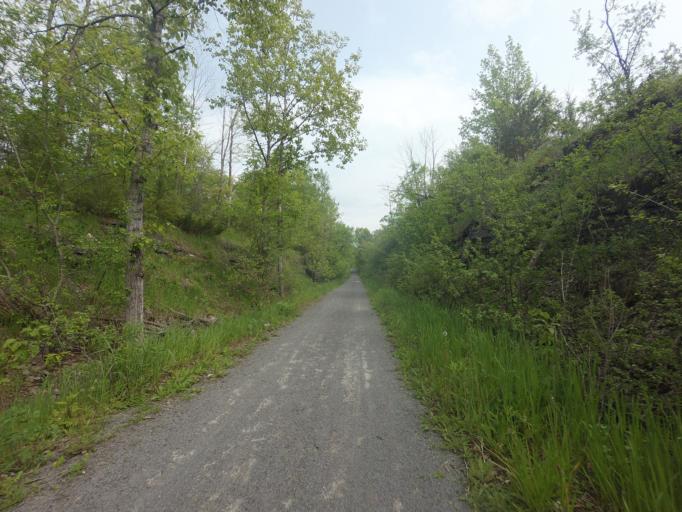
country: CA
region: Ontario
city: Kingston
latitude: 44.4122
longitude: -76.6208
